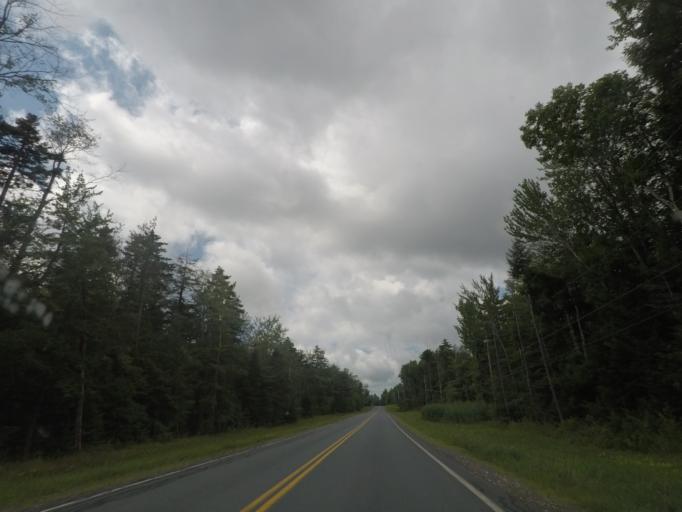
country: US
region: New York
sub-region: Rensselaer County
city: Poestenkill
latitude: 42.6979
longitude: -73.4090
